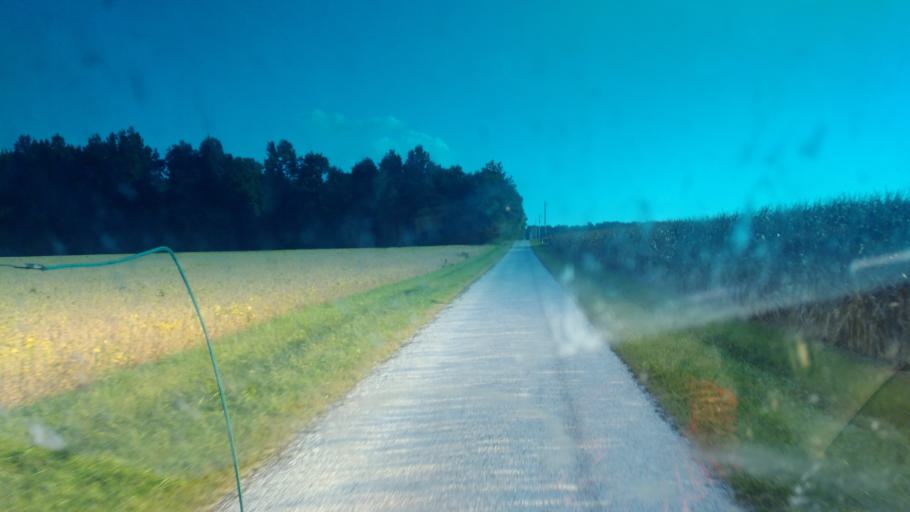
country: US
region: Ohio
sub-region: Crawford County
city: Bucyrus
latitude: 40.9299
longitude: -82.9973
